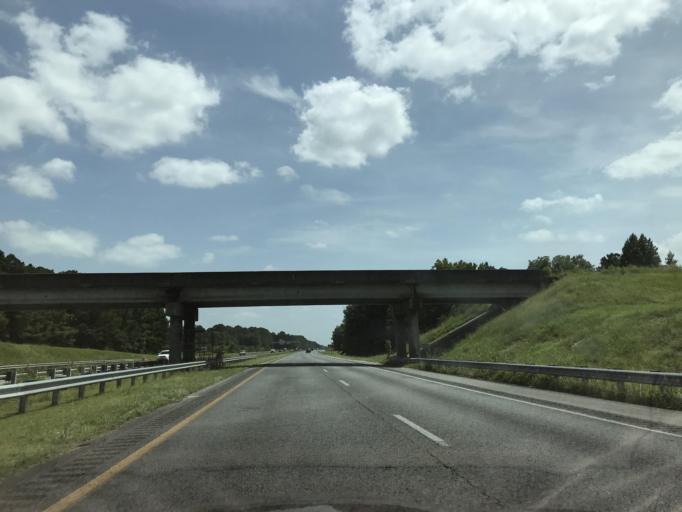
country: US
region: North Carolina
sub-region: Duplin County
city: Kenansville
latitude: 34.9182
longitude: -78.0250
